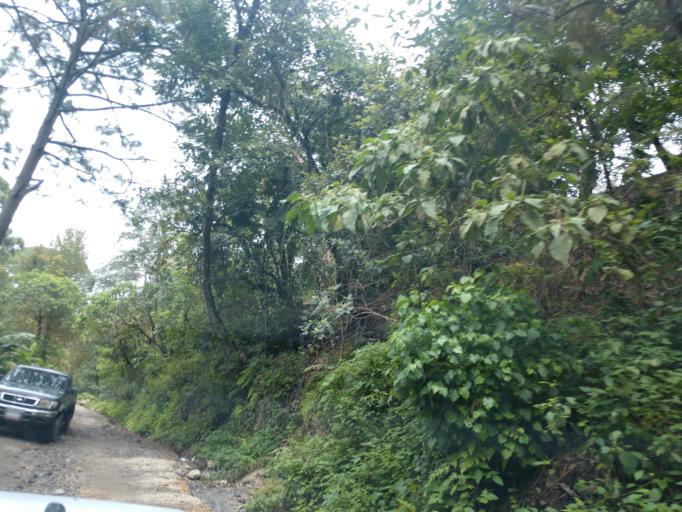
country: MX
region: Nayarit
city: Xalisco
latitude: 21.4353
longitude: -104.9362
